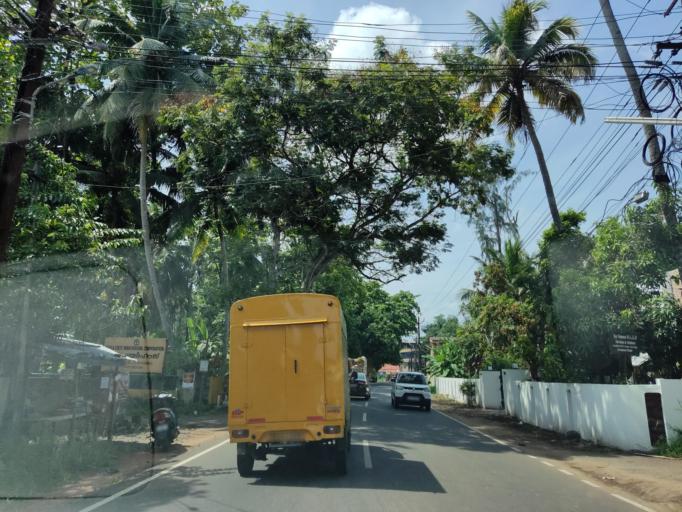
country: IN
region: Kerala
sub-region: Alappuzha
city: Mavelikara
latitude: 9.2755
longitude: 76.5364
